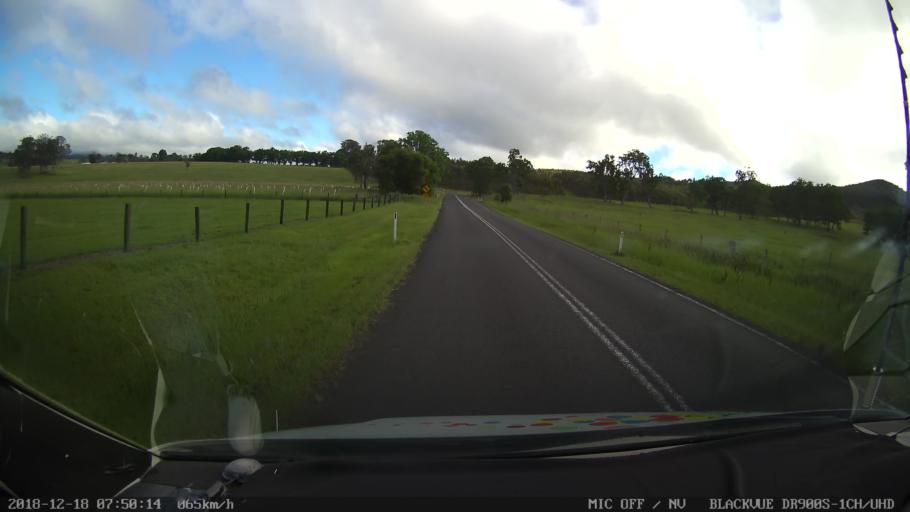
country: AU
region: New South Wales
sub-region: Kyogle
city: Kyogle
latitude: -28.4473
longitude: 152.5739
